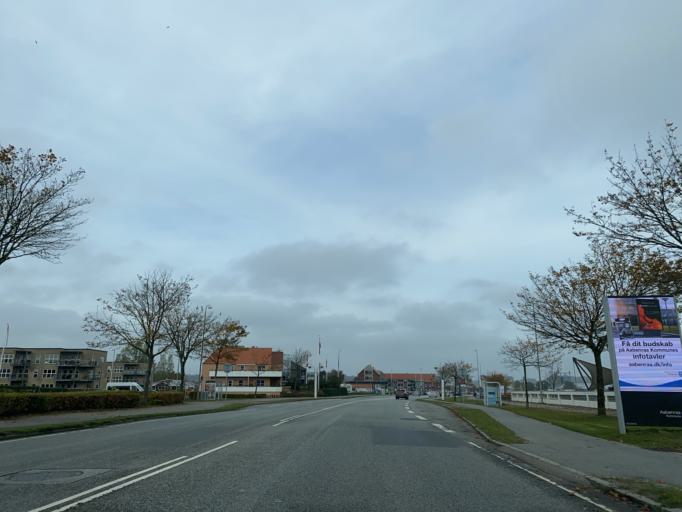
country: DK
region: South Denmark
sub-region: Aabenraa Kommune
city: Aabenraa
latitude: 55.0332
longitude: 9.4205
